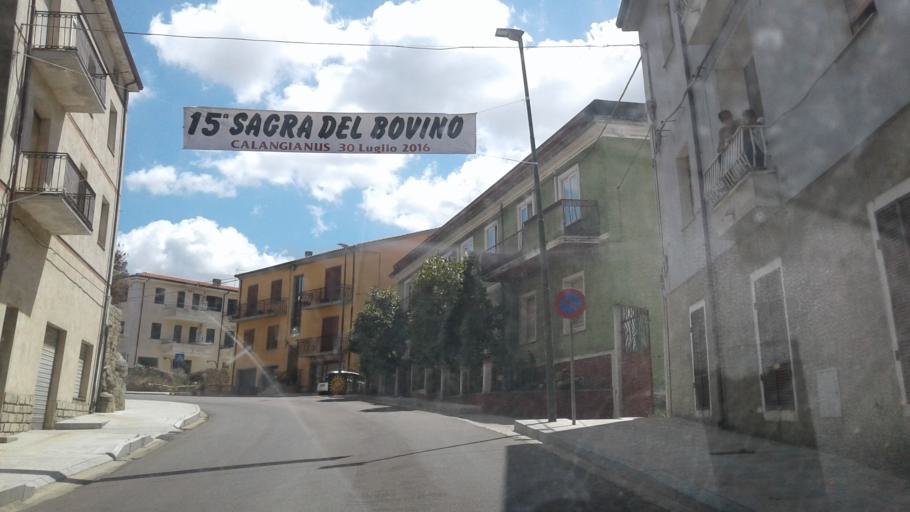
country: IT
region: Sardinia
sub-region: Provincia di Olbia-Tempio
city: Calangianus
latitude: 40.9203
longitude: 9.1912
